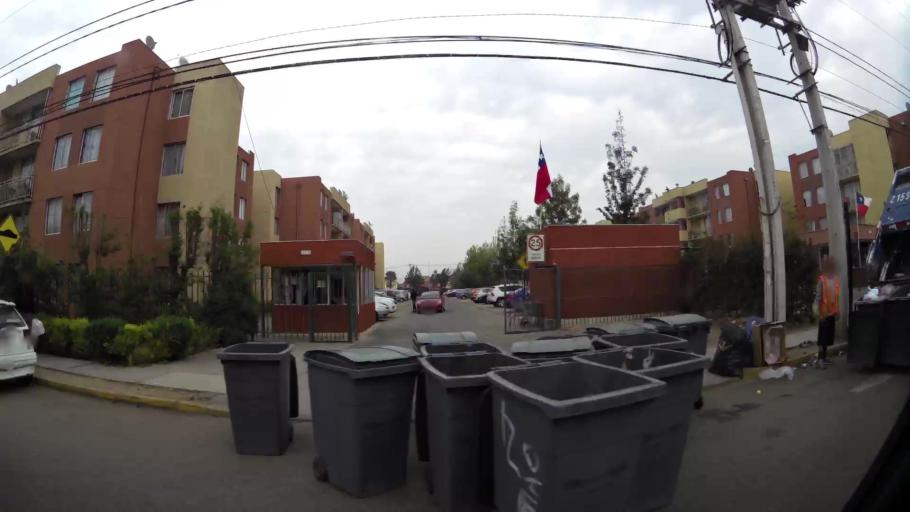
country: CL
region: Santiago Metropolitan
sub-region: Provincia de Santiago
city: Lo Prado
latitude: -33.4866
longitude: -70.7402
